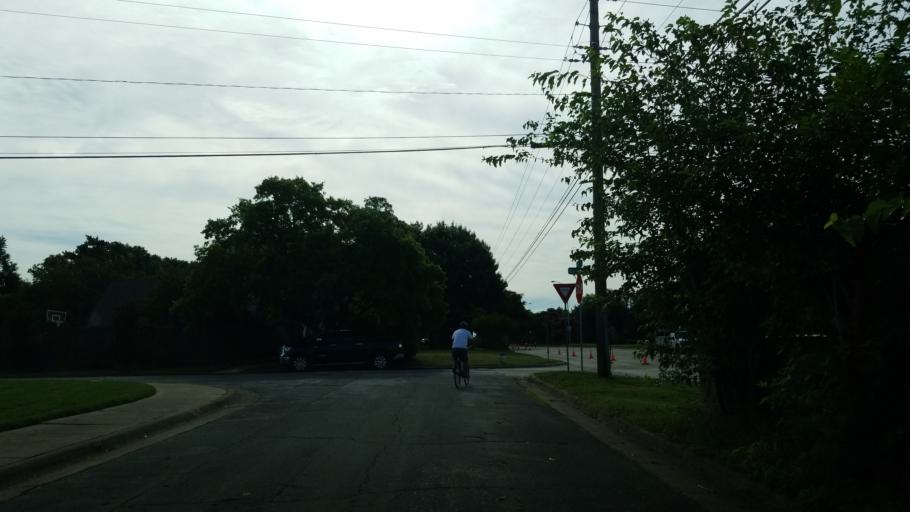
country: US
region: Texas
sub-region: Dallas County
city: Farmers Branch
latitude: 32.8952
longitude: -96.8471
